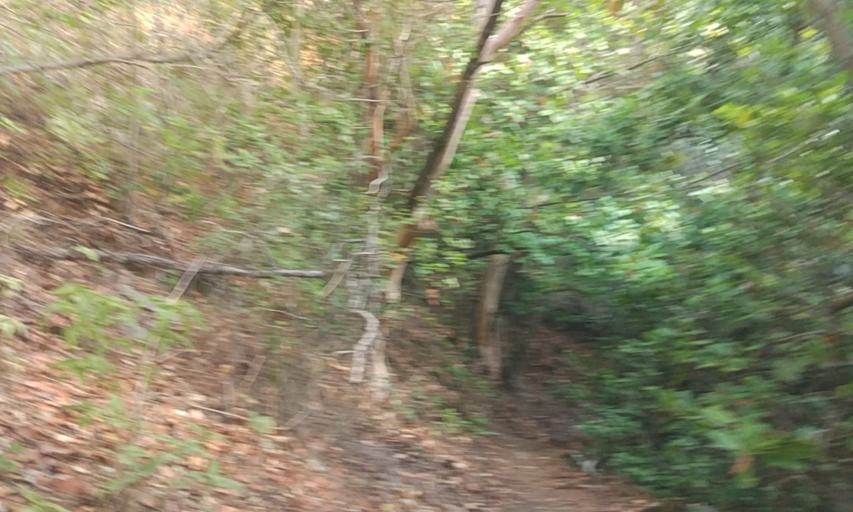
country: TR
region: Antalya
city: Tekirova
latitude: 36.3806
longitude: 30.4763
